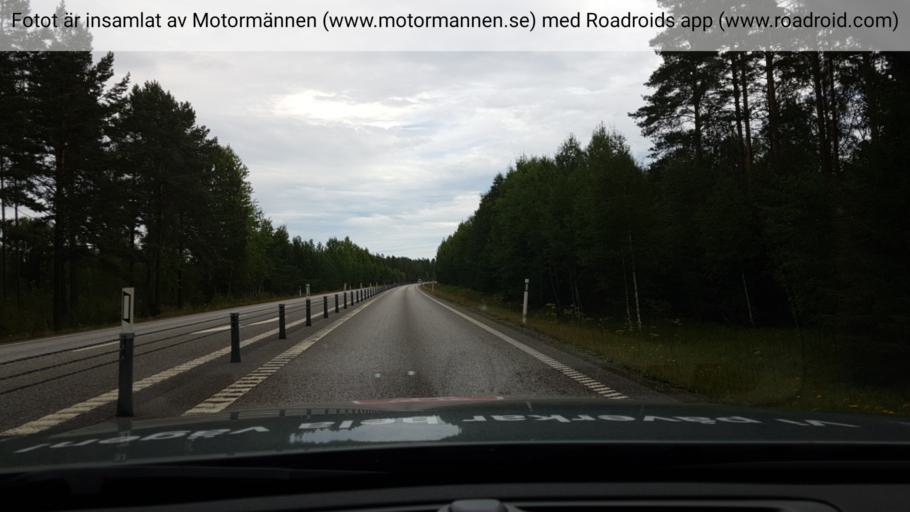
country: SE
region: Uppsala
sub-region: Heby Kommun
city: Tarnsjo
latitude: 60.1440
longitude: 16.9303
